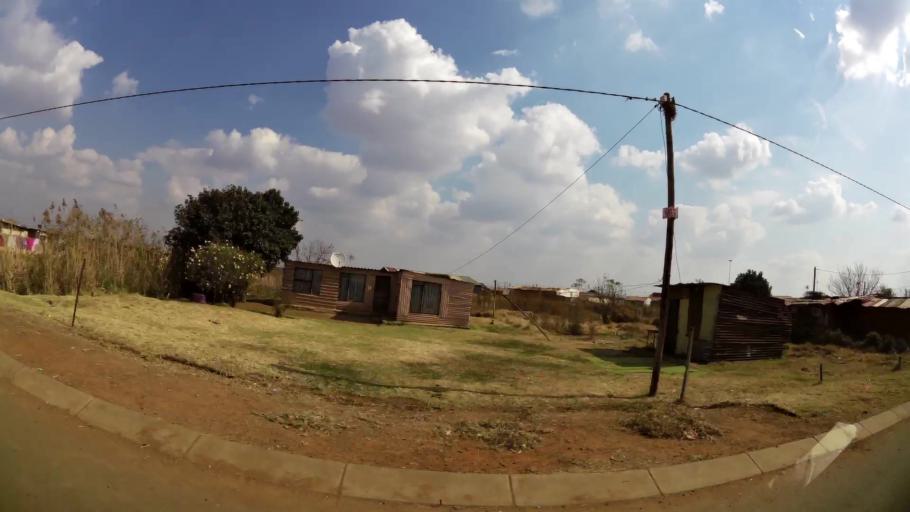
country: ZA
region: Gauteng
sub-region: Ekurhuleni Metropolitan Municipality
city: Springs
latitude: -26.1325
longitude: 28.4761
